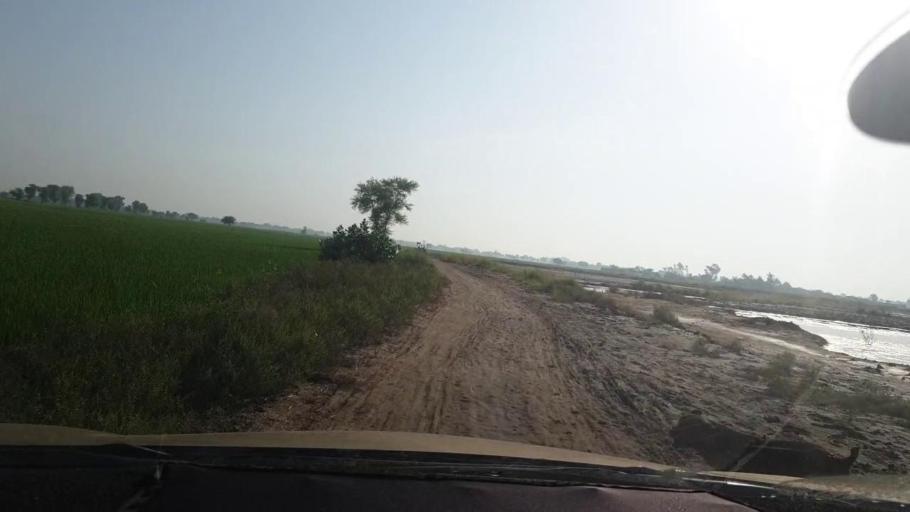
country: PK
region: Sindh
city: Kambar
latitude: 27.6424
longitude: 68.0471
